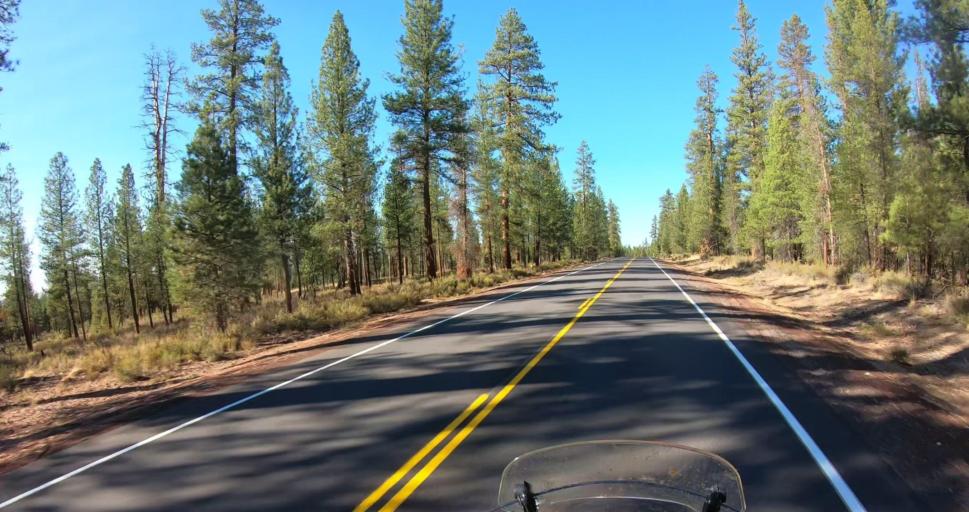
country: US
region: Oregon
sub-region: Deschutes County
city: La Pine
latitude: 43.5080
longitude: -121.4508
